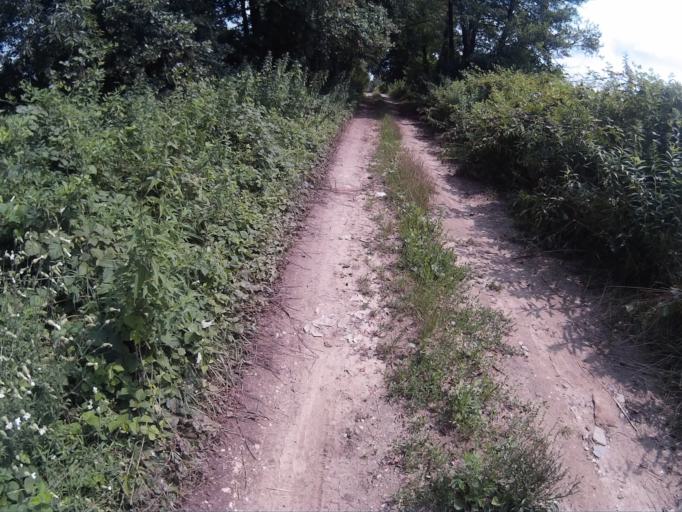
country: HU
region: Veszprem
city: Papa
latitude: 47.2936
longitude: 17.5910
